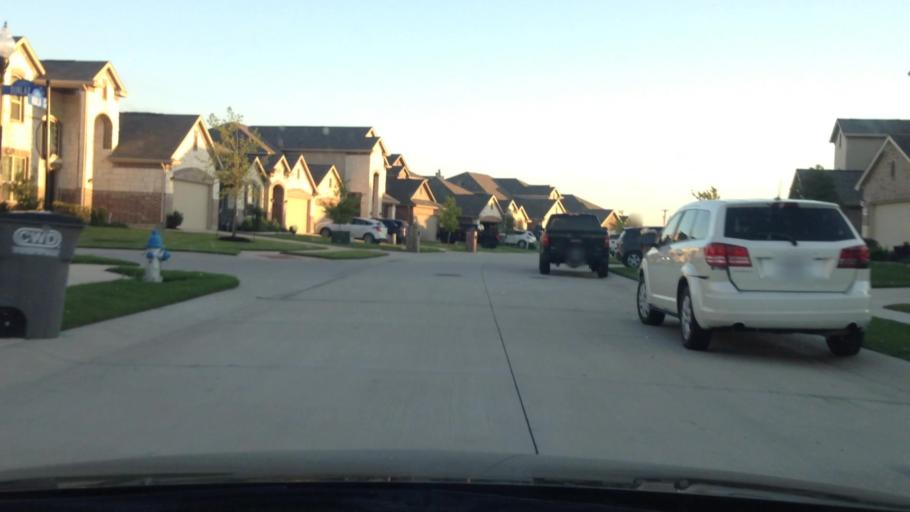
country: US
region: Texas
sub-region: Denton County
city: Little Elm
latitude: 33.1385
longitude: -96.9325
